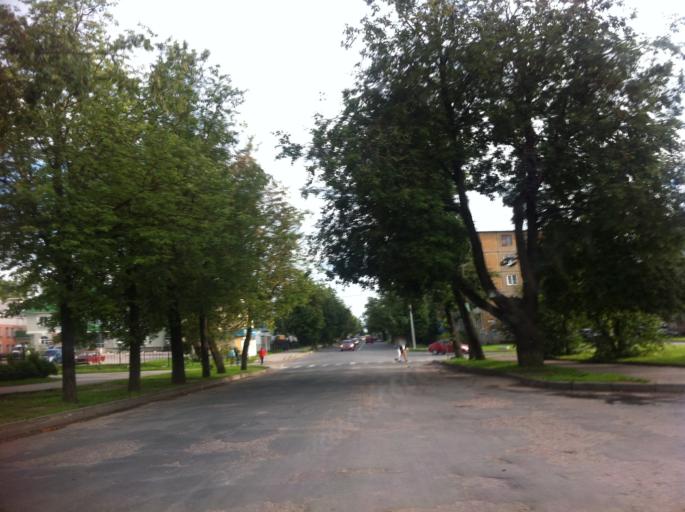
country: RU
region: Pskov
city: Pskov
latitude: 57.8220
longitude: 28.3200
